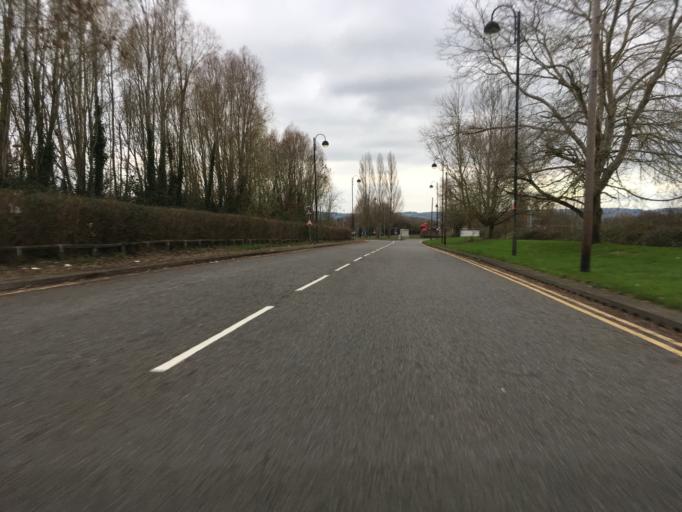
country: GB
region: Wales
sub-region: Newport
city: Bishton
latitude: 51.5757
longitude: -2.8637
